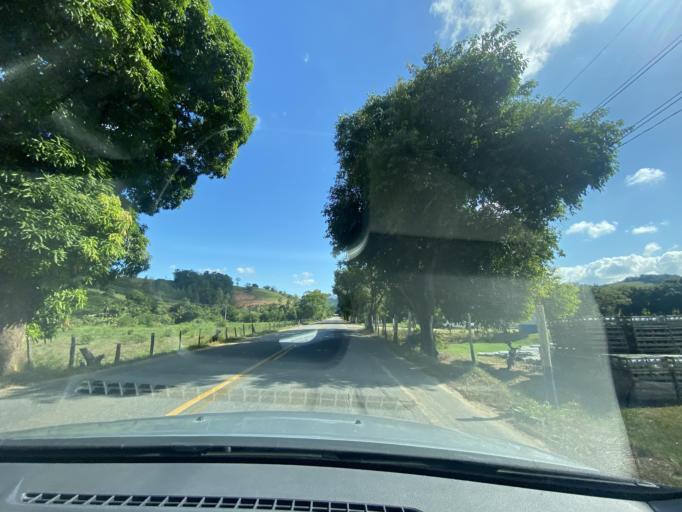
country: BR
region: Espirito Santo
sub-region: Jeronimo Monteiro
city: Jeronimo Monteiro
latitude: -20.7898
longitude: -41.4105
